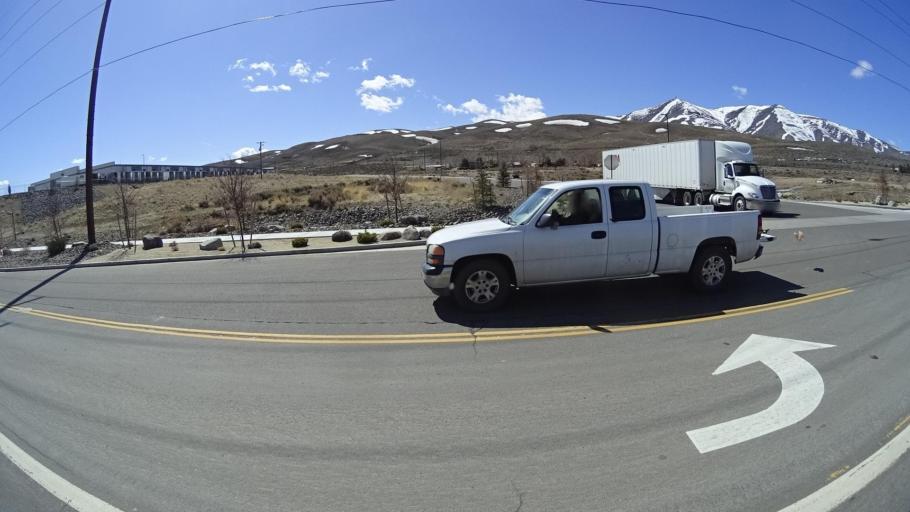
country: US
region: Nevada
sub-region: Washoe County
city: Lemmon Valley
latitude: 39.6162
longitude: -119.8750
